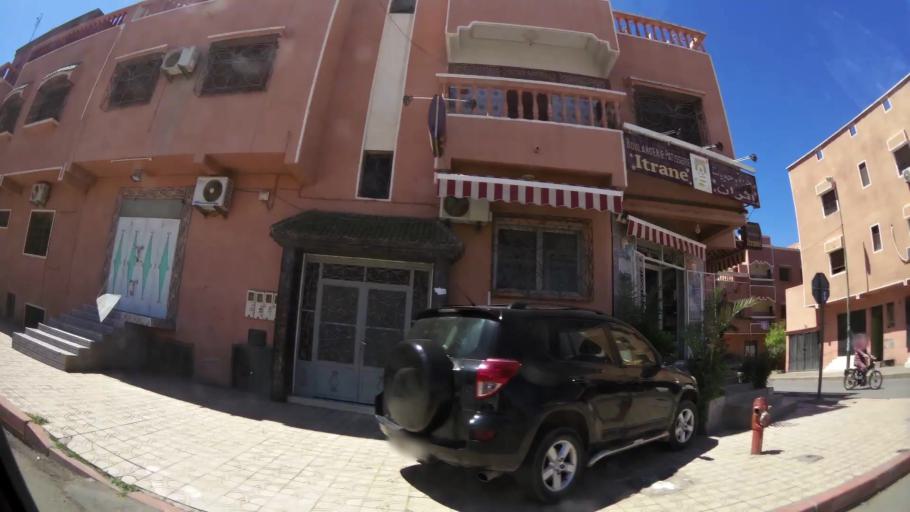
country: MA
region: Marrakech-Tensift-Al Haouz
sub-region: Marrakech
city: Marrakesh
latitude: 31.6582
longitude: -7.9886
